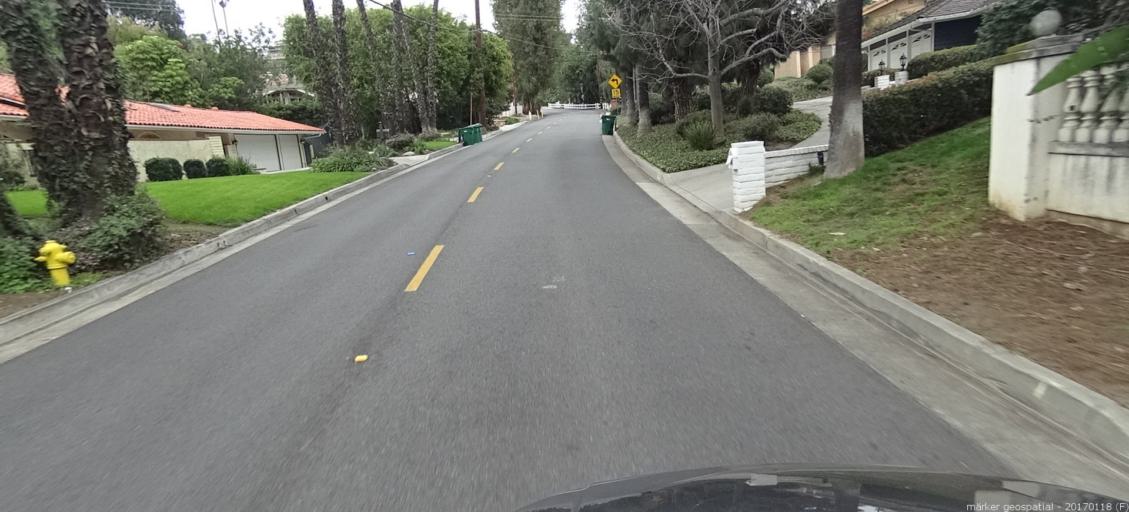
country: US
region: California
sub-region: Orange County
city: North Tustin
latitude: 33.7541
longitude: -117.7852
